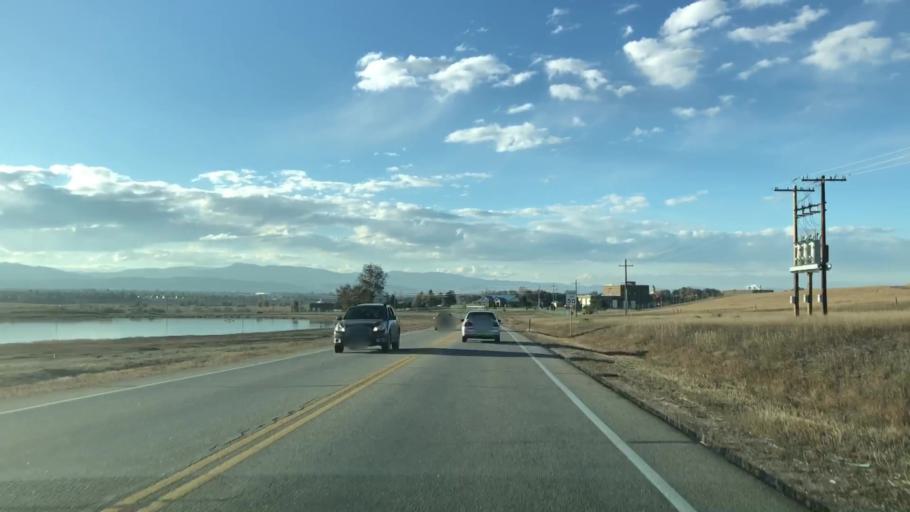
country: US
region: Colorado
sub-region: Larimer County
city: Loveland
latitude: 40.4813
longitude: -105.0245
